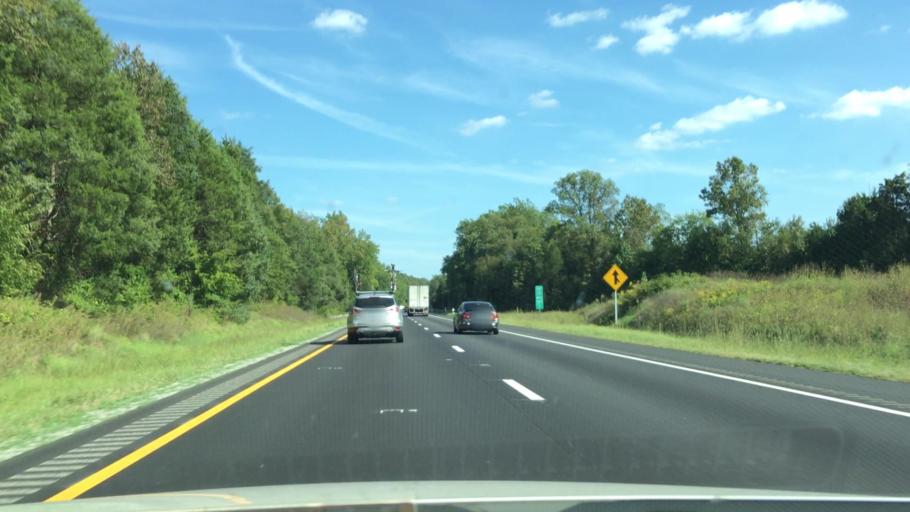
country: US
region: Virginia
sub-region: Goochland County
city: Goochland
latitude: 37.7102
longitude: -77.7822
